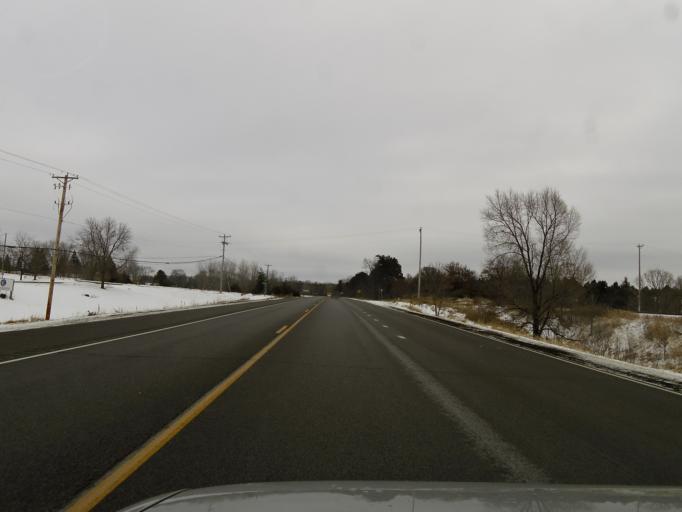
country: US
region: Minnesota
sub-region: Washington County
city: Lake Elmo
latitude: 44.9964
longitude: -92.8998
